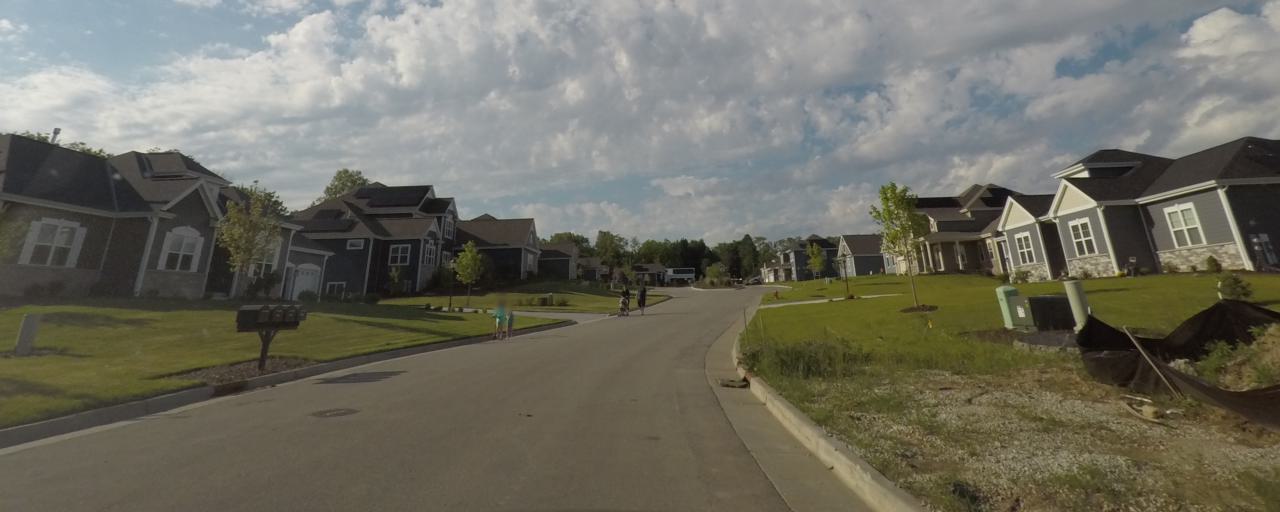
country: US
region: Wisconsin
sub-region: Waukesha County
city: New Berlin
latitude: 42.9416
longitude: -88.0922
